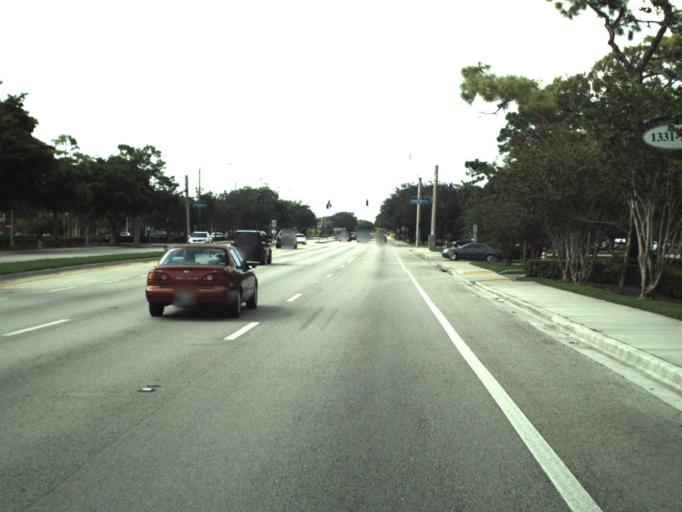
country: US
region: Florida
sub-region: Broward County
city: Coral Springs
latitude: 26.2468
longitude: -80.2531
